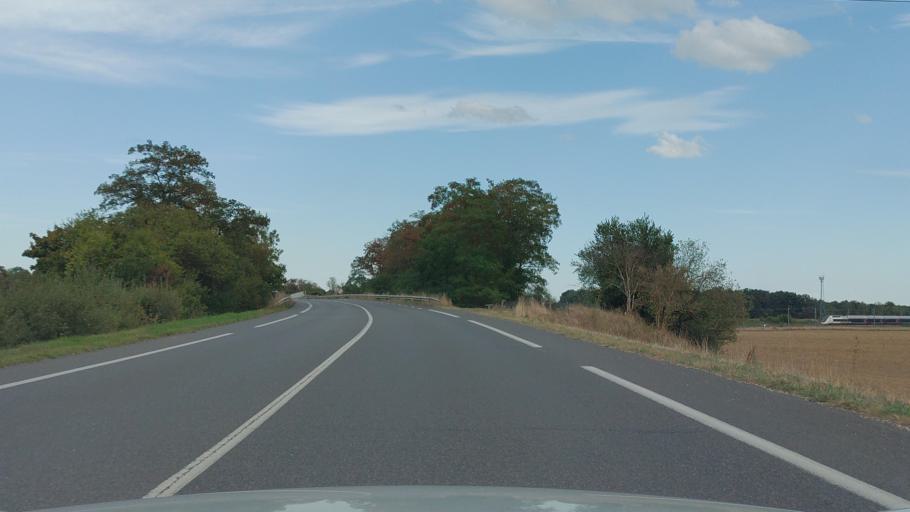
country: FR
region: Ile-de-France
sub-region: Departement de Seine-et-Marne
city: Le Chatelet-en-Brie
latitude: 48.5461
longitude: 2.7779
